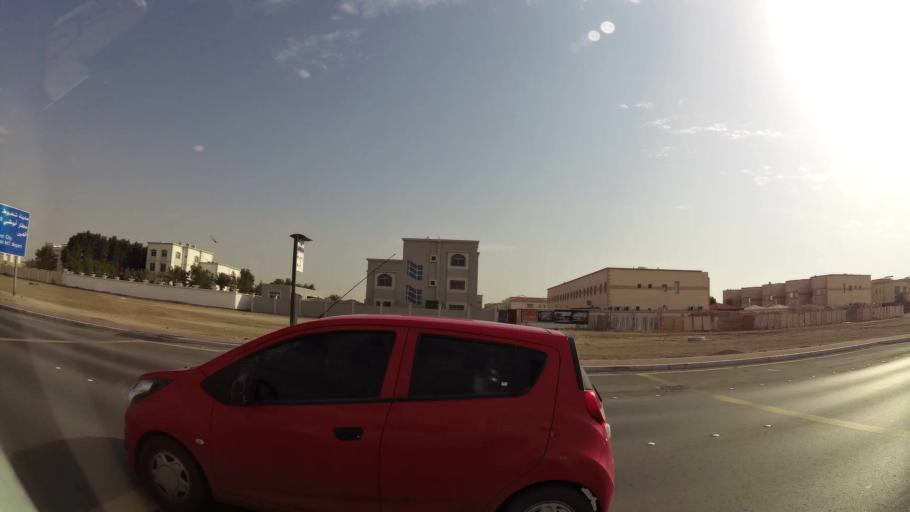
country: AE
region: Abu Dhabi
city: Abu Dhabi
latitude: 24.3260
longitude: 54.5711
